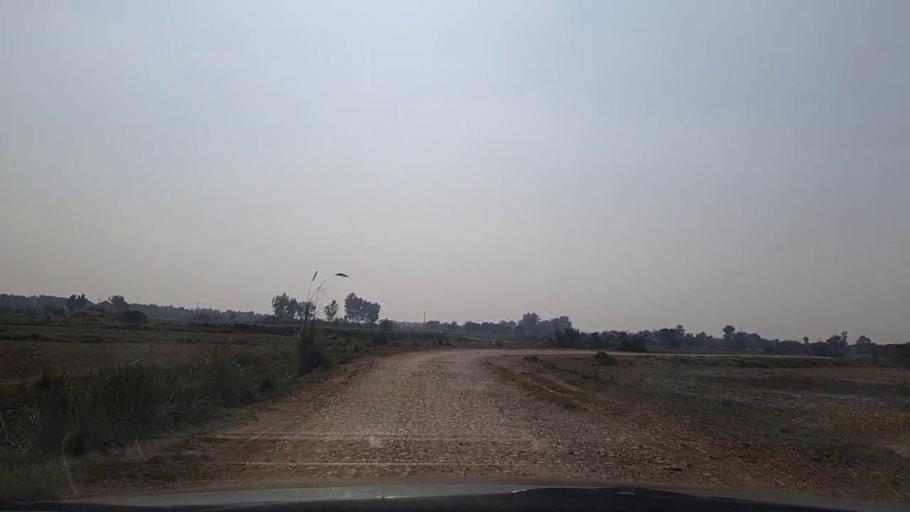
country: PK
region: Sindh
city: Mirpur Sakro
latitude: 24.5648
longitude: 67.7775
